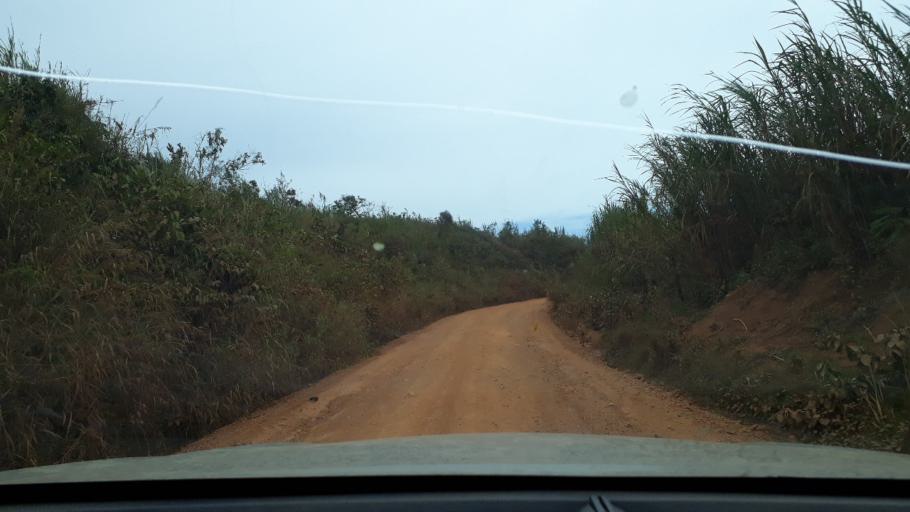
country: CD
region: Eastern Province
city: Bunia
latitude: 1.8413
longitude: 30.4591
